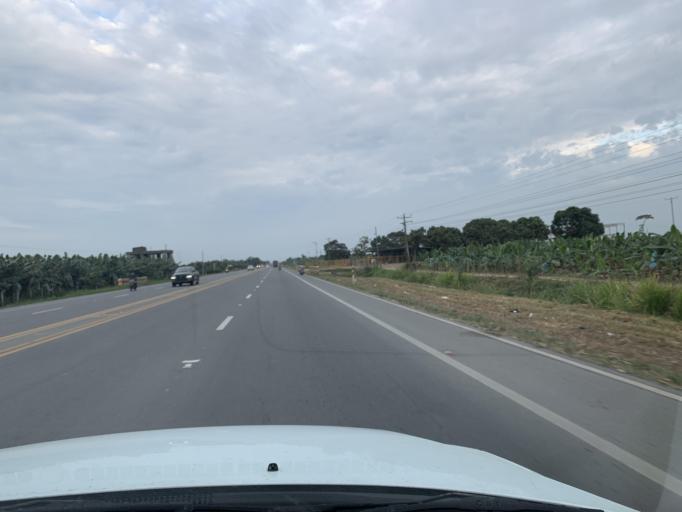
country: EC
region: Guayas
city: Naranjito
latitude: -2.2551
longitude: -79.6137
